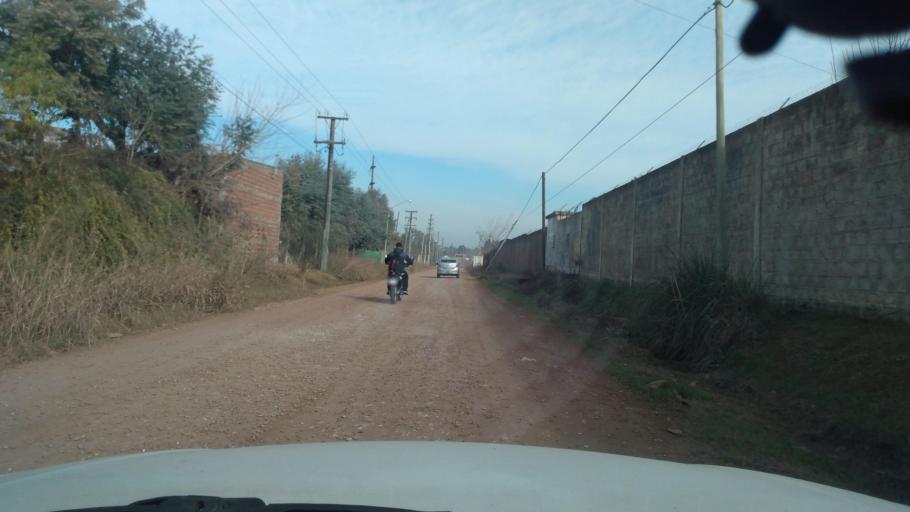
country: AR
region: Buenos Aires
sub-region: Partido de Lujan
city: Lujan
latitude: -34.5851
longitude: -59.1192
